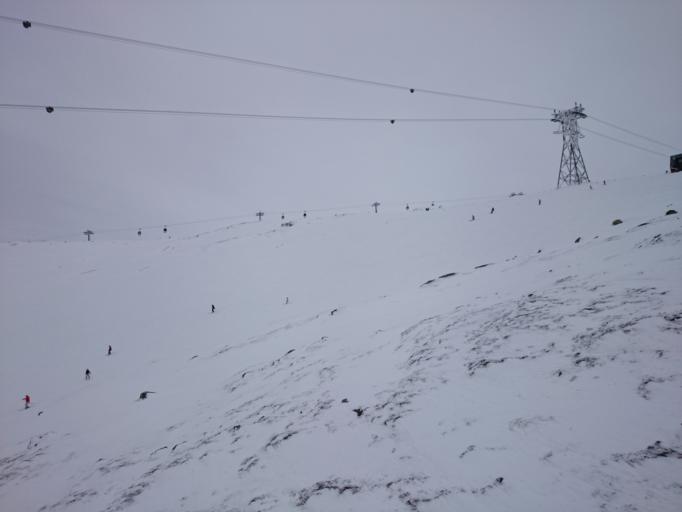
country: SE
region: Jaemtland
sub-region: Are Kommun
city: Are
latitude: 63.4237
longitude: 13.0811
